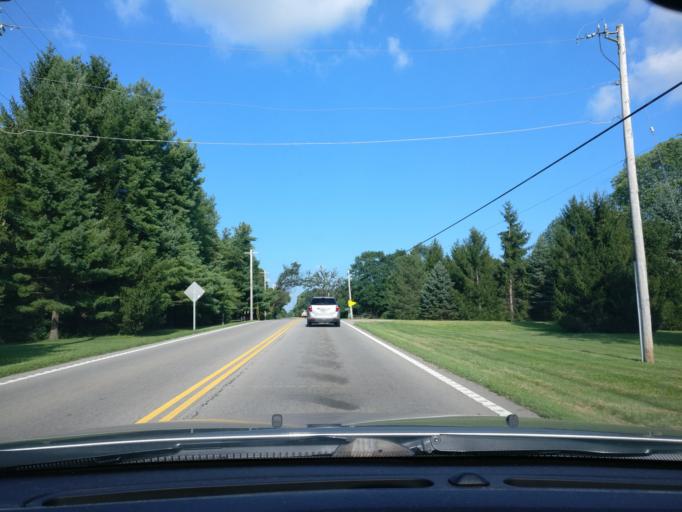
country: US
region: Ohio
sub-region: Warren County
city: Five Points
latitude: 39.5454
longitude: -84.1804
